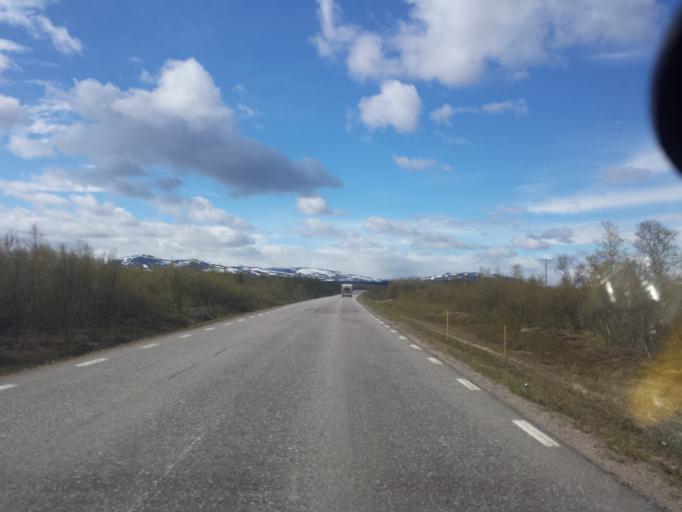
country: SE
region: Norrbotten
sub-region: Kiruna Kommun
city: Kiruna
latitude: 68.0001
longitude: 19.8620
